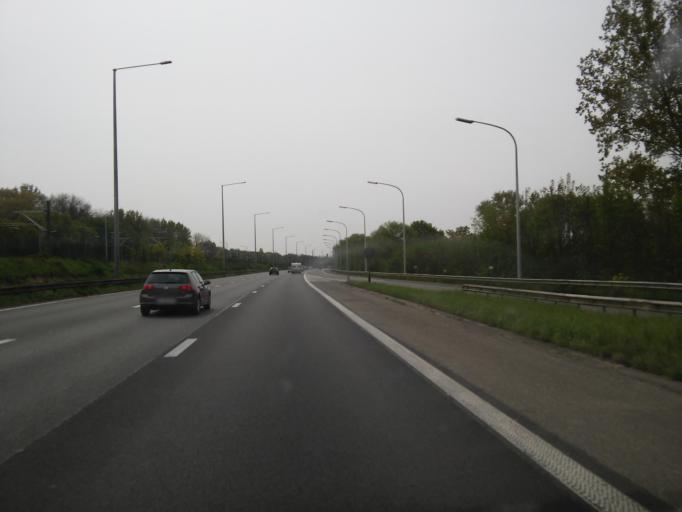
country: BE
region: Flanders
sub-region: Provincie Vlaams-Brabant
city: Zemst
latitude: 50.9733
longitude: 4.4896
